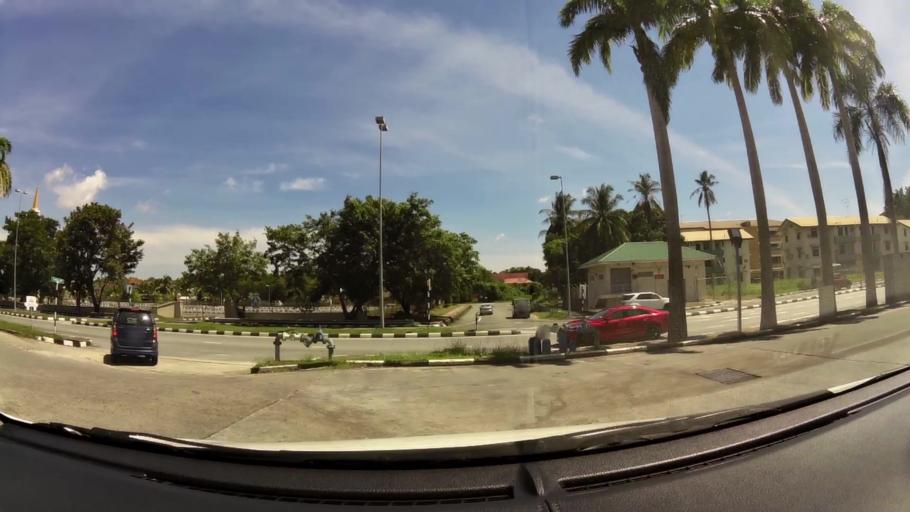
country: BN
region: Brunei and Muara
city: Bandar Seri Begawan
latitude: 4.9443
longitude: 114.9465
